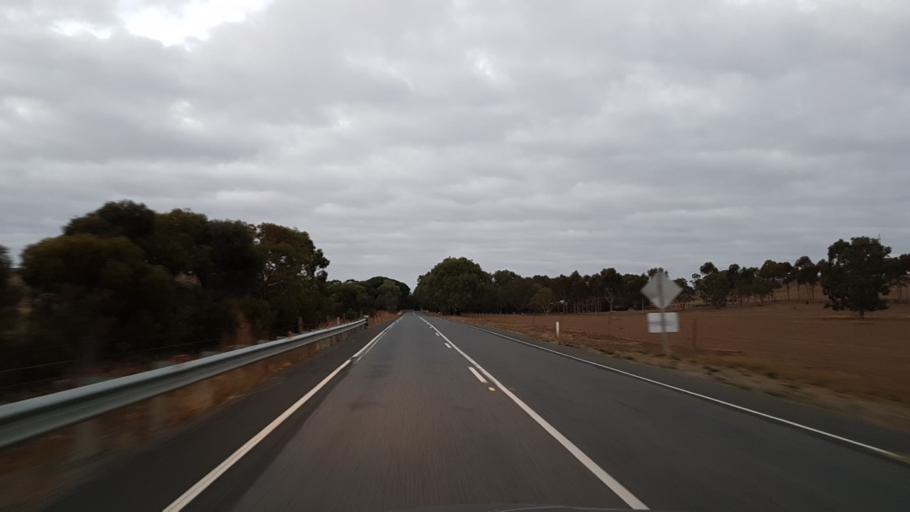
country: AU
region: South Australia
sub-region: Mount Barker
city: Callington
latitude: -35.0559
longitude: 139.0105
